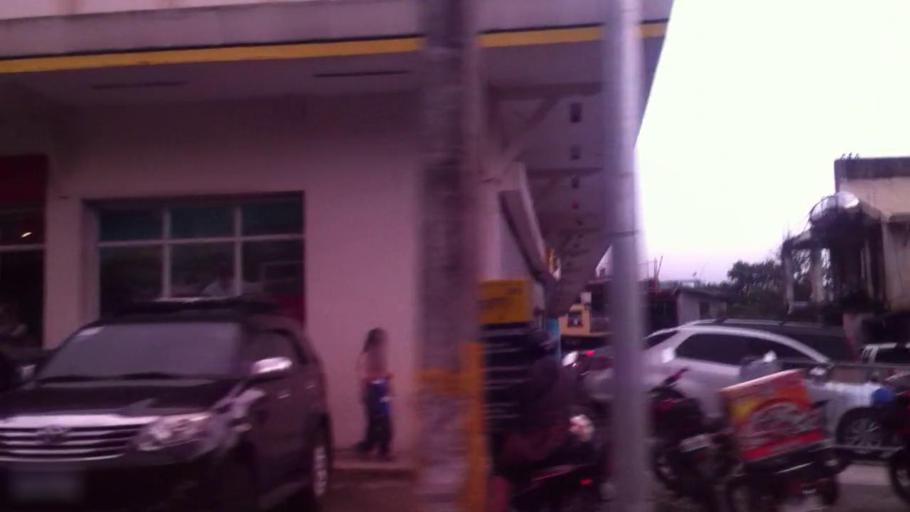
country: PH
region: Cordillera
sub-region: Province of Benguet
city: La Trinidad
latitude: 16.4448
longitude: 120.5914
